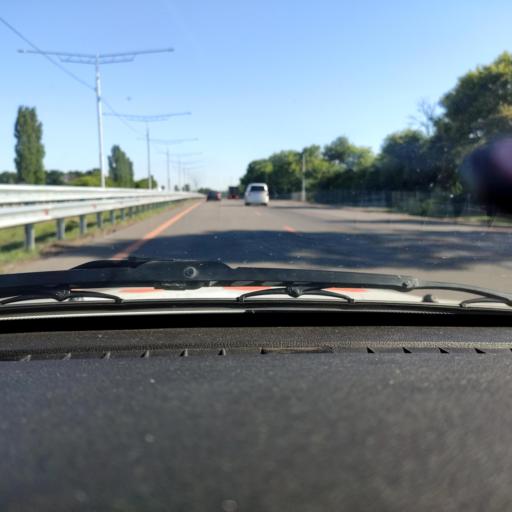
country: RU
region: Voronezj
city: Ramon'
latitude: 51.9660
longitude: 39.2235
